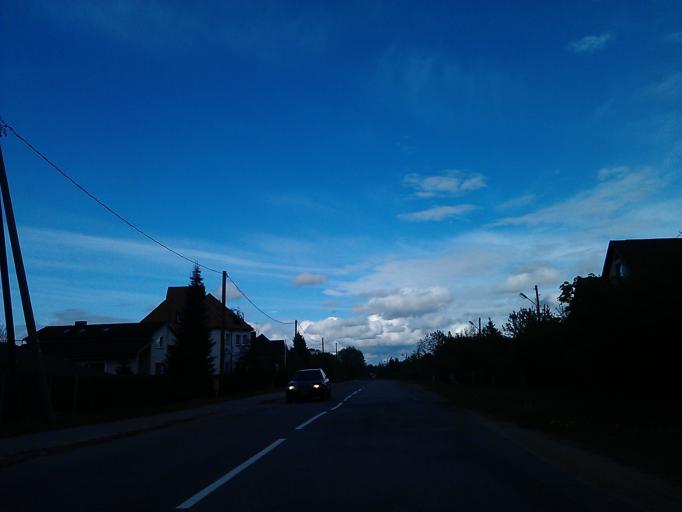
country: LV
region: Adazi
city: Adazi
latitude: 57.0692
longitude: 24.3323
